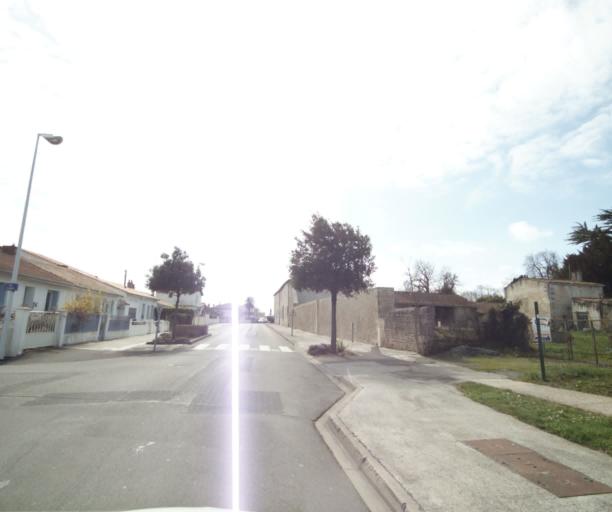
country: FR
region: Poitou-Charentes
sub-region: Departement de la Charente-Maritime
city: Lagord
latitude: 46.1801
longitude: -1.1591
